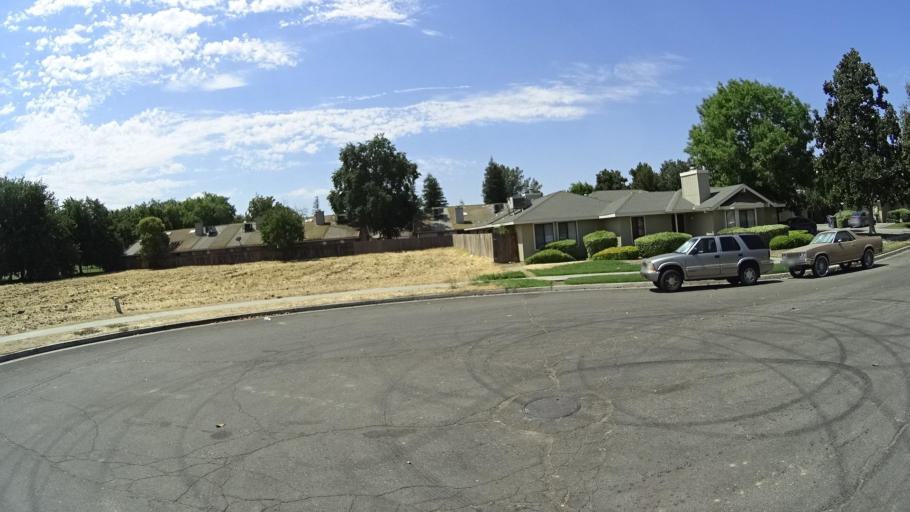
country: US
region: California
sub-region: Fresno County
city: Sunnyside
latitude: 36.7306
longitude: -119.7167
